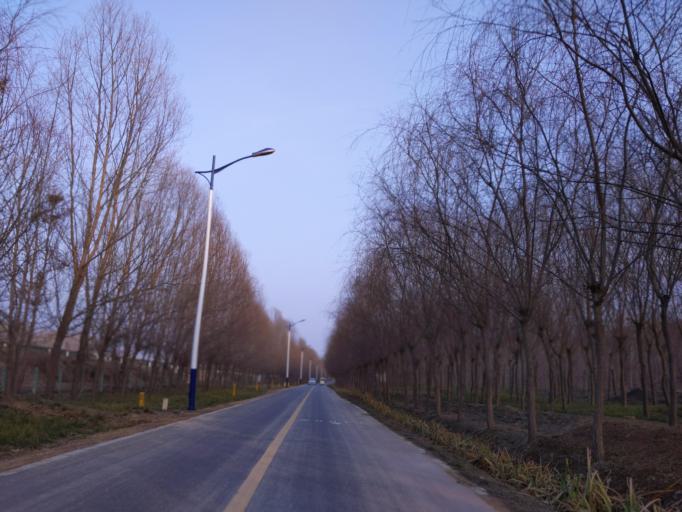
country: CN
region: Henan Sheng
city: Puyang
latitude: 35.8212
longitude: 115.0146
